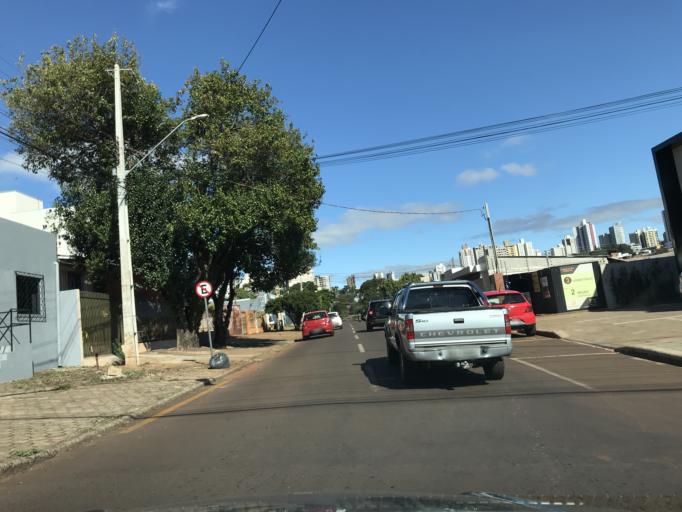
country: BR
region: Parana
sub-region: Cascavel
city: Cascavel
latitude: -24.9434
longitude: -53.4686
